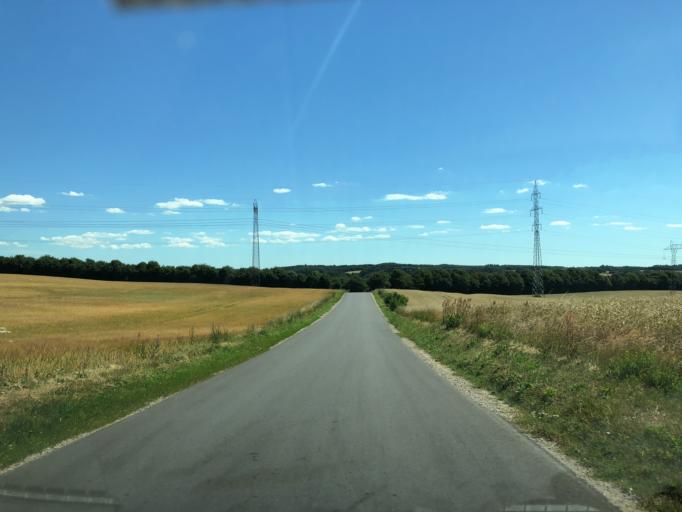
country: DK
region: Central Jutland
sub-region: Viborg Kommune
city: Bjerringbro
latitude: 56.5116
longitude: 9.5602
